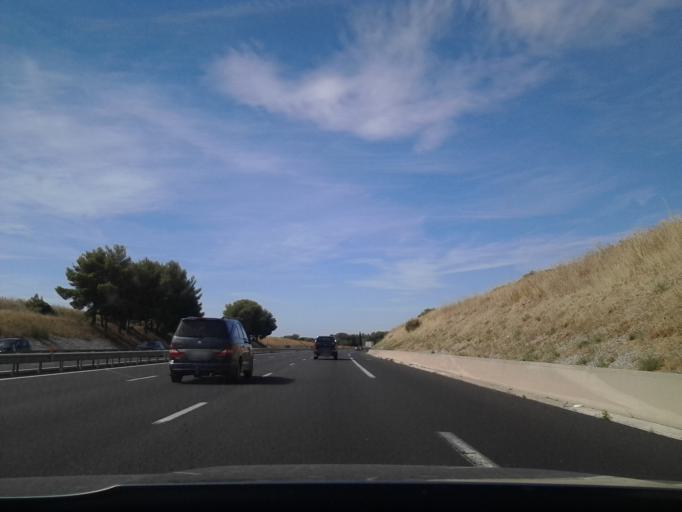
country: FR
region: Languedoc-Roussillon
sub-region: Departement de l'Herault
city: Meze
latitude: 43.4329
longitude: 3.5636
